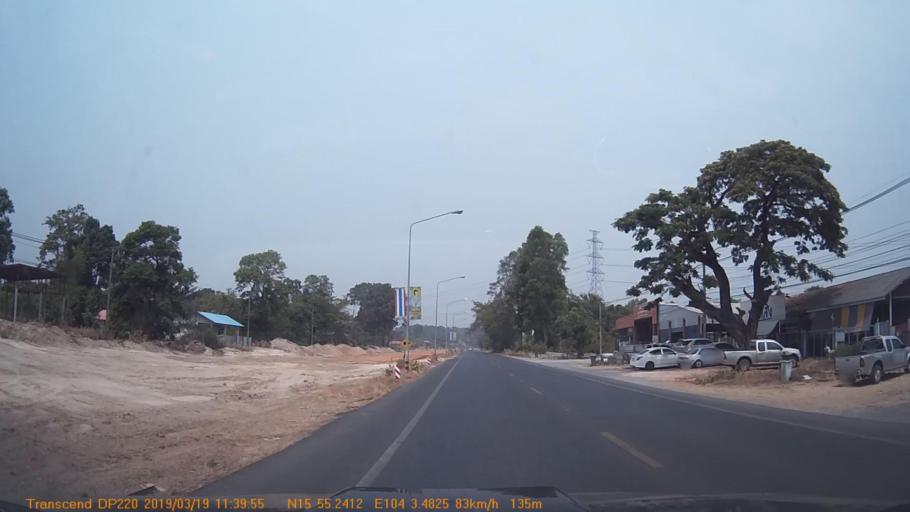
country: TH
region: Roi Et
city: Ban Selaphum
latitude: 15.9209
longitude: 104.0579
